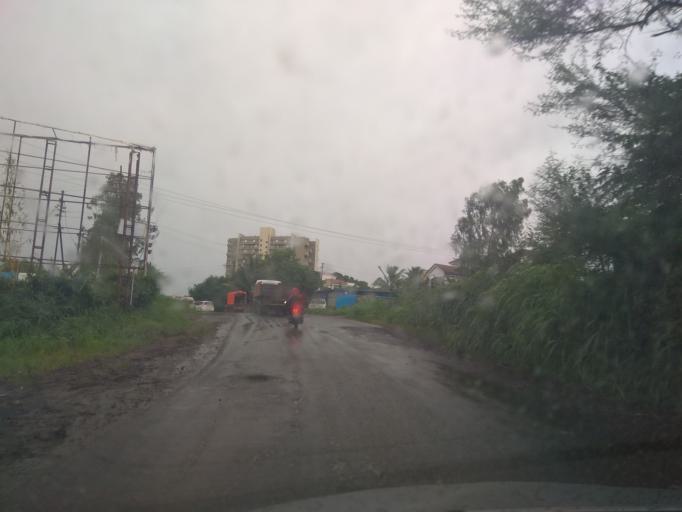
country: IN
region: Maharashtra
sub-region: Pune Division
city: Kharakvasla
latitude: 18.5143
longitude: 73.6618
